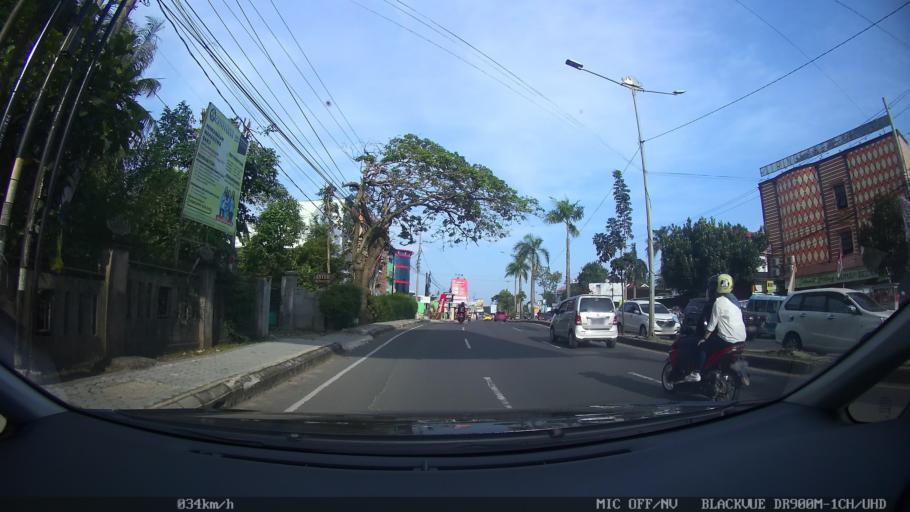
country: ID
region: Lampung
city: Kedaton
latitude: -5.3759
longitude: 105.2472
